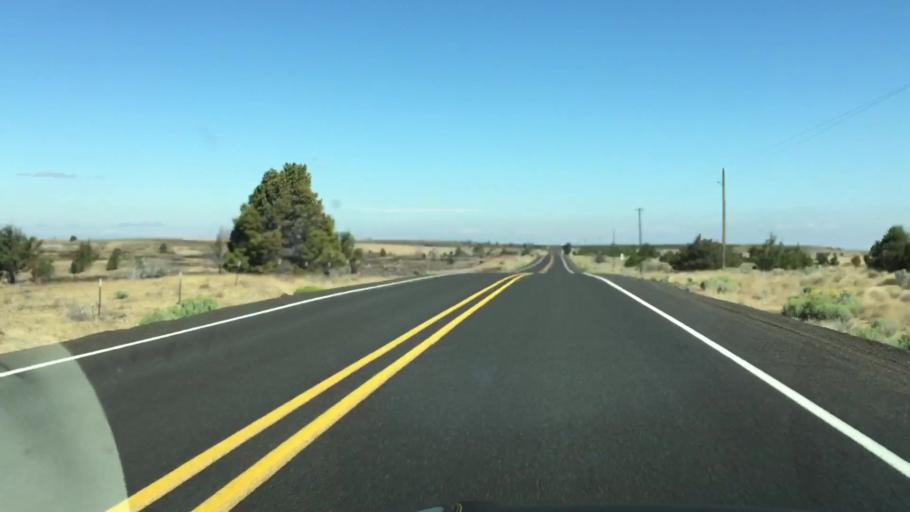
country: US
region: Oregon
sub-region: Jefferson County
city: Warm Springs
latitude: 45.0311
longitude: -120.9941
